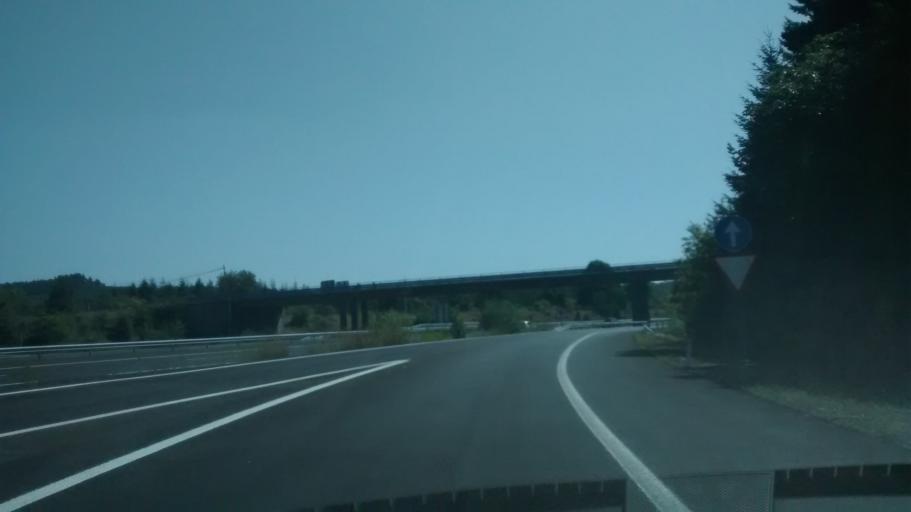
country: ES
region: Basque Country
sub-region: Provincia de Alava
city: Murguia
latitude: 42.9635
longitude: -2.8697
